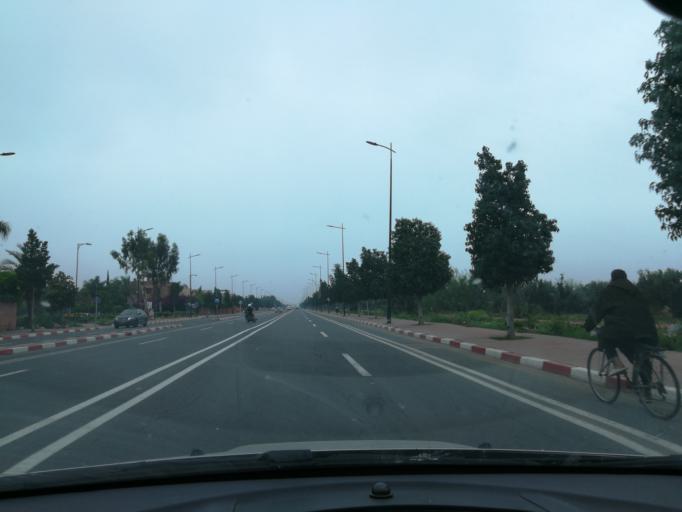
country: MA
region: Marrakech-Tensift-Al Haouz
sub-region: Marrakech
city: Marrakesh
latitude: 31.6141
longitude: -7.9966
